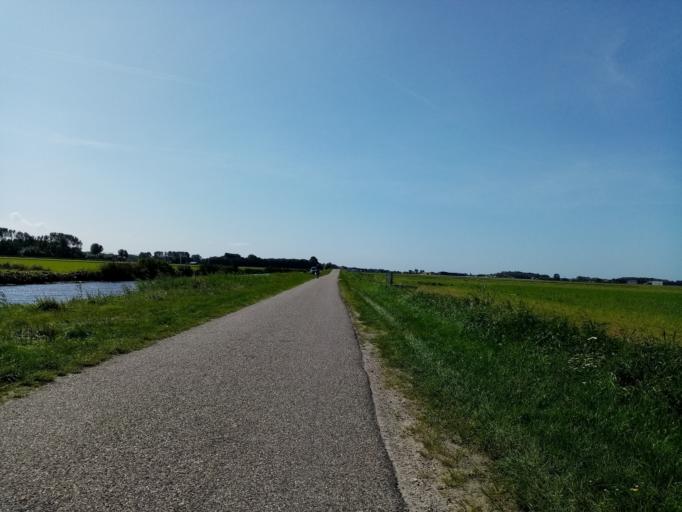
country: NL
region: South Holland
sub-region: Gemeente Lisse
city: Lisse
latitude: 52.2917
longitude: 4.5488
